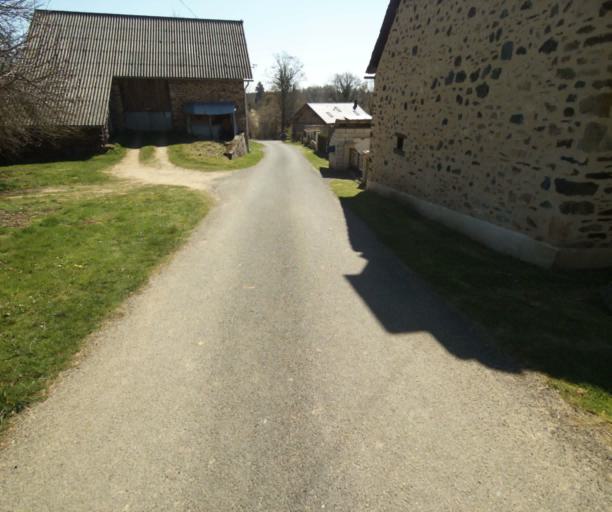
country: FR
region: Limousin
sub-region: Departement de la Correze
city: Saint-Clement
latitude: 45.3215
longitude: 1.6939
